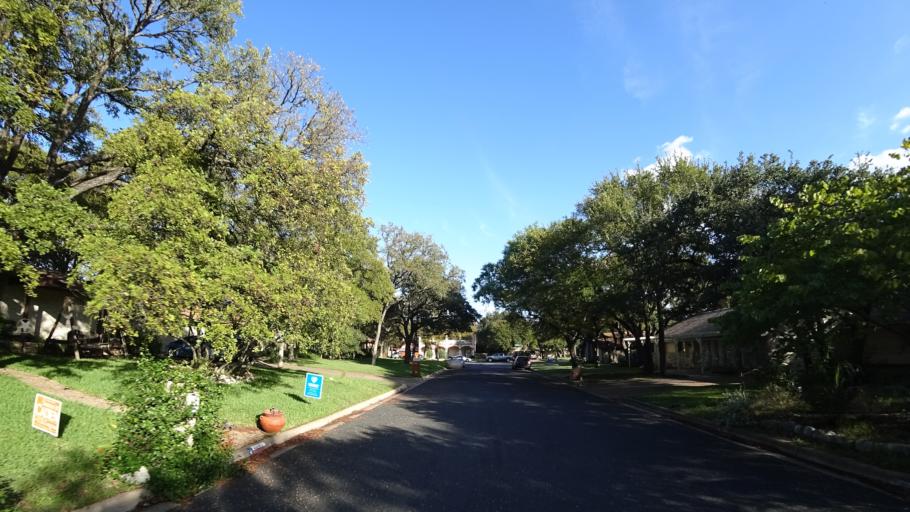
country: US
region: Texas
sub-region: Williamson County
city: Jollyville
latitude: 30.3661
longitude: -97.7475
